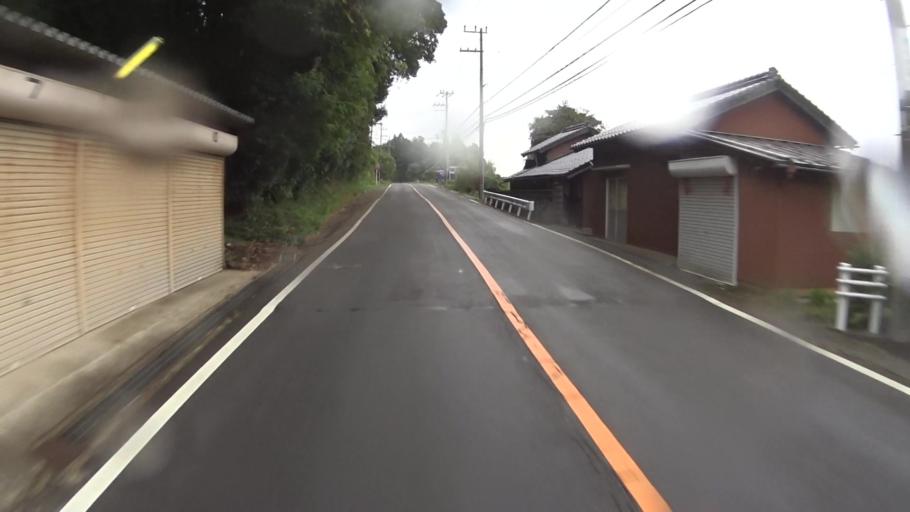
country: JP
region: Kyoto
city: Miyazu
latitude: 35.5561
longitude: 135.2368
